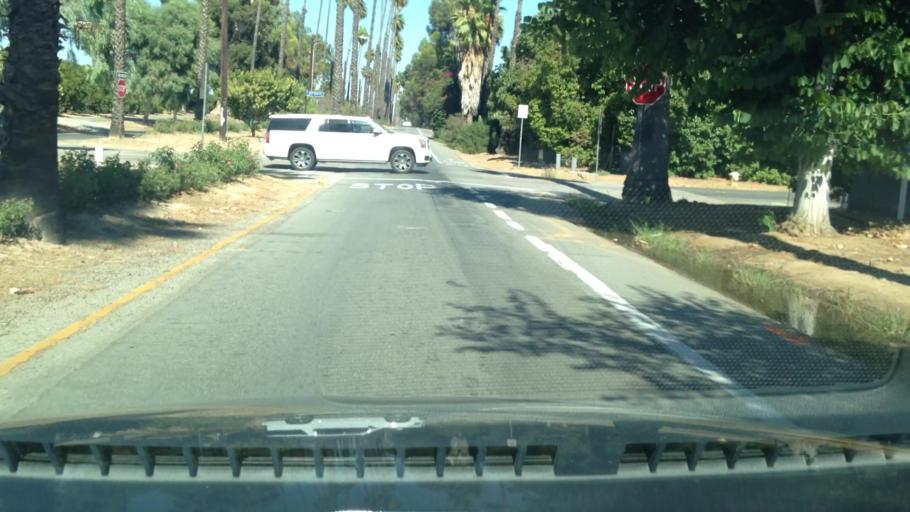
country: US
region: California
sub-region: Riverside County
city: Riverside
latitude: 33.9087
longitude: -117.4266
